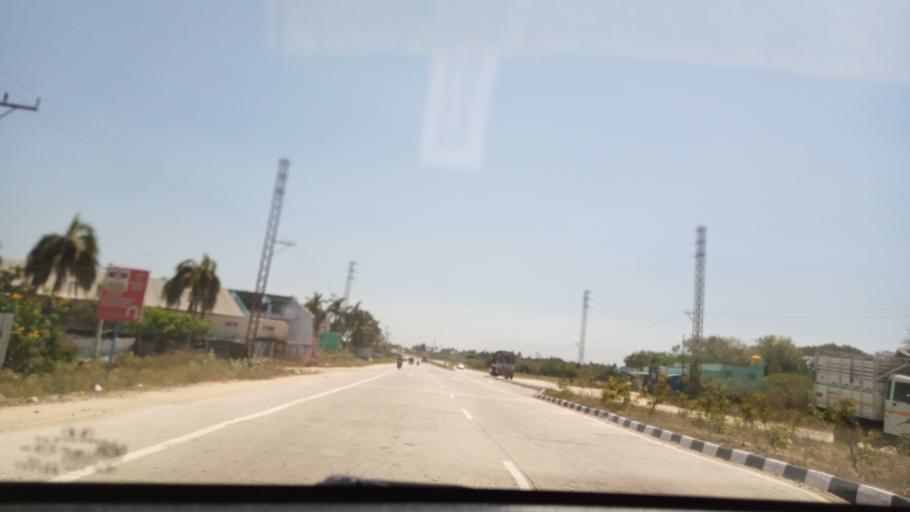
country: IN
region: Andhra Pradesh
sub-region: Chittoor
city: Chittoor
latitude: 13.2038
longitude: 78.9467
